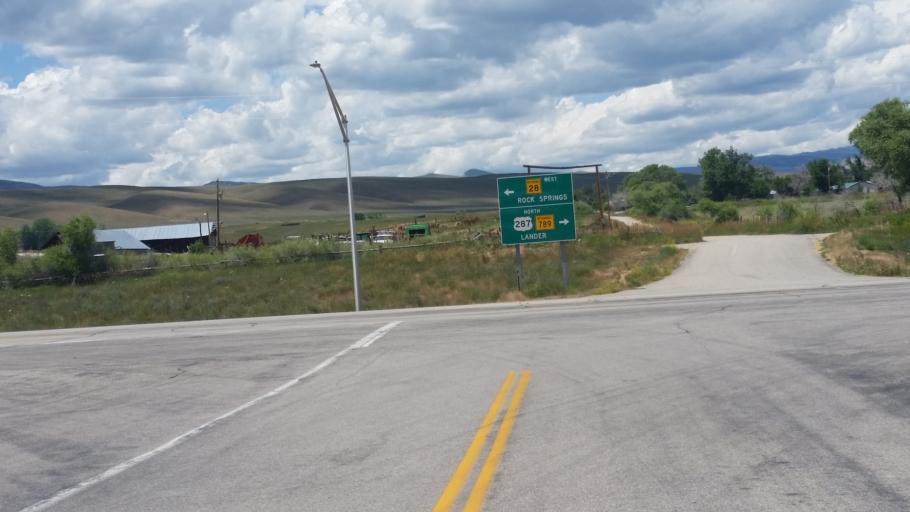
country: US
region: Wyoming
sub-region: Fremont County
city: Lander
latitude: 42.7288
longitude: -108.6460
